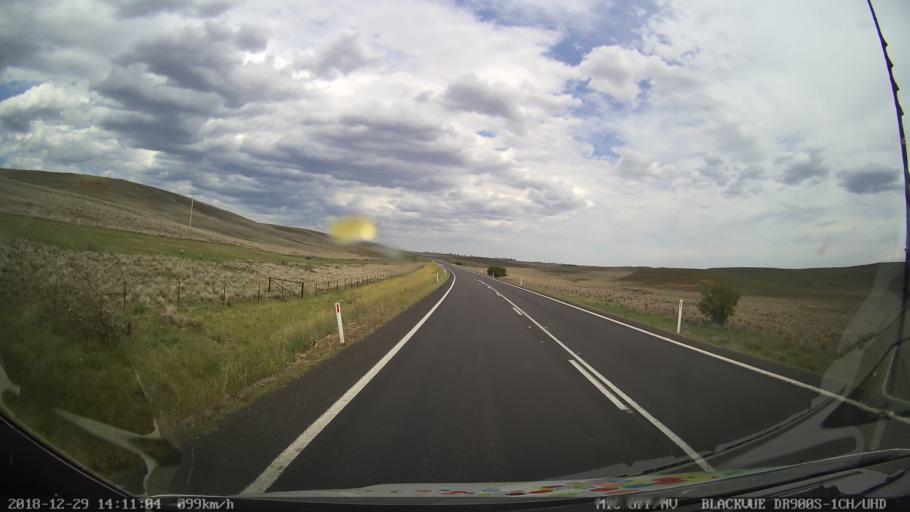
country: AU
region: New South Wales
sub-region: Cooma-Monaro
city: Cooma
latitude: -36.4007
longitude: 149.2178
